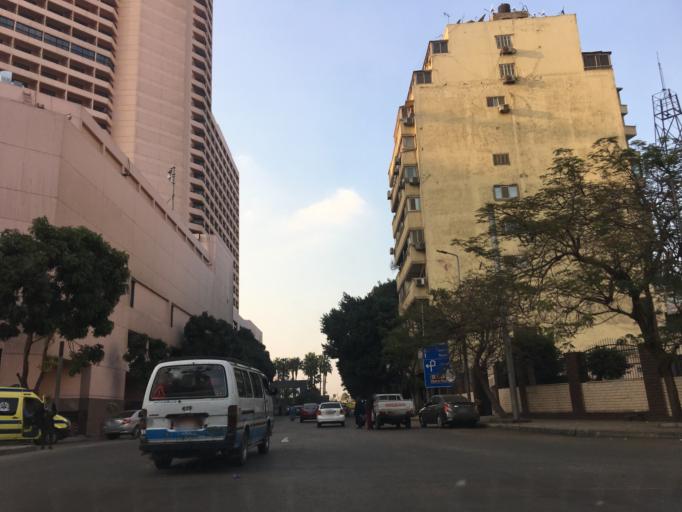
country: EG
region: Muhafazat al Qahirah
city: Cairo
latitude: 30.0424
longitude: 31.2333
